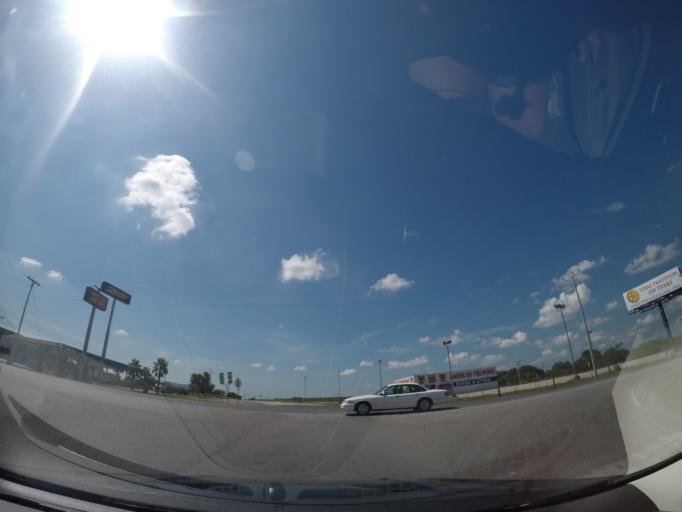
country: US
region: Texas
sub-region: Guadalupe County
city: McQueeney
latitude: 29.5411
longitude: -98.0725
